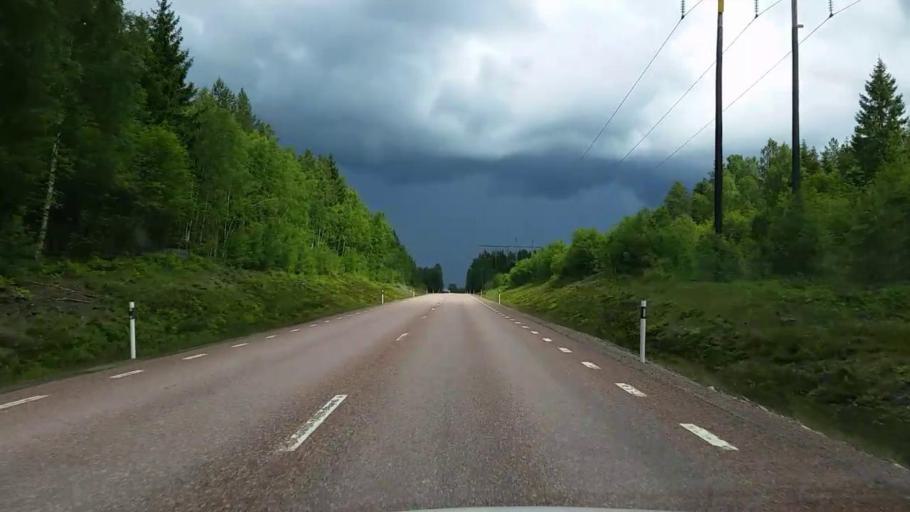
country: SE
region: Gaevleborg
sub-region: Hofors Kommun
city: Hofors
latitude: 60.5429
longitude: 16.4662
